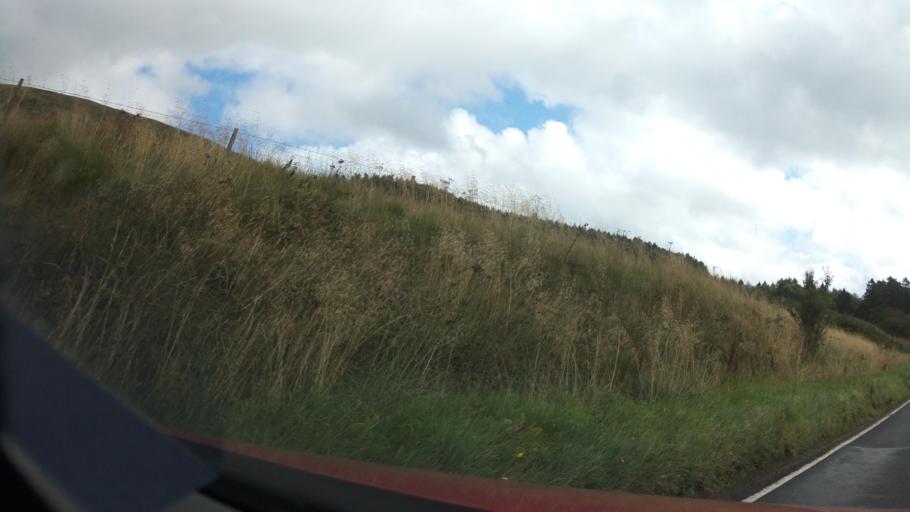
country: GB
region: Scotland
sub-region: The Scottish Borders
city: Jedburgh
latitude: 55.3366
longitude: -2.4471
